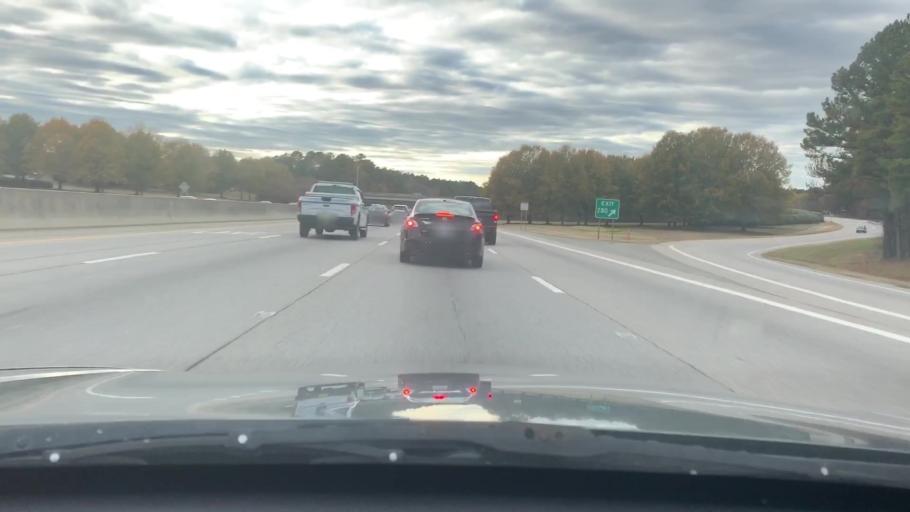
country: US
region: North Carolina
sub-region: Wake County
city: Morrisville
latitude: 35.8938
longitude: -78.8564
